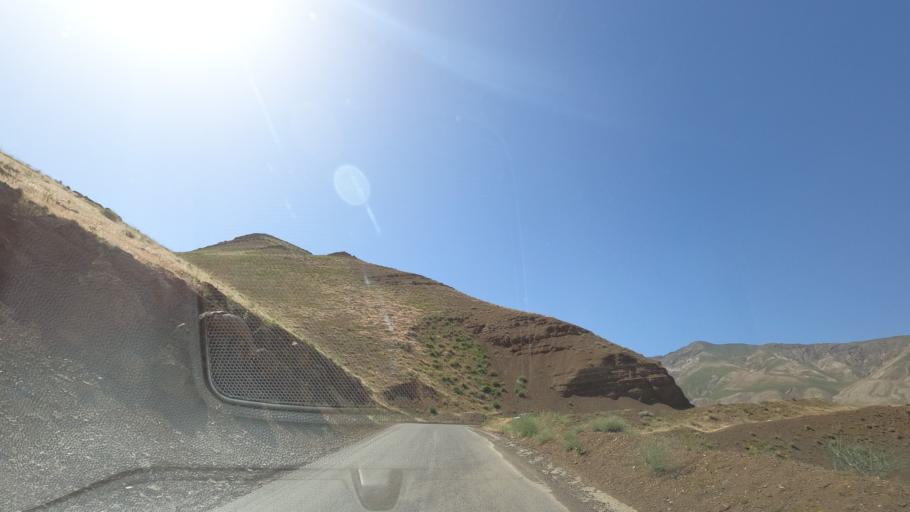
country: IR
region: Alborz
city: Karaj
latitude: 35.9374
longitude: 51.0805
